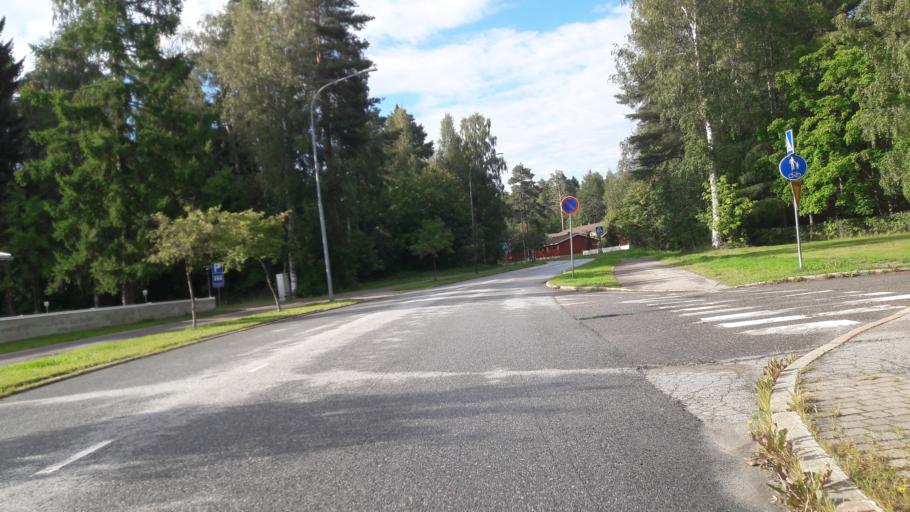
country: FI
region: North Karelia
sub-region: Joensuu
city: Joensuu
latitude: 62.5801
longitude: 29.7894
